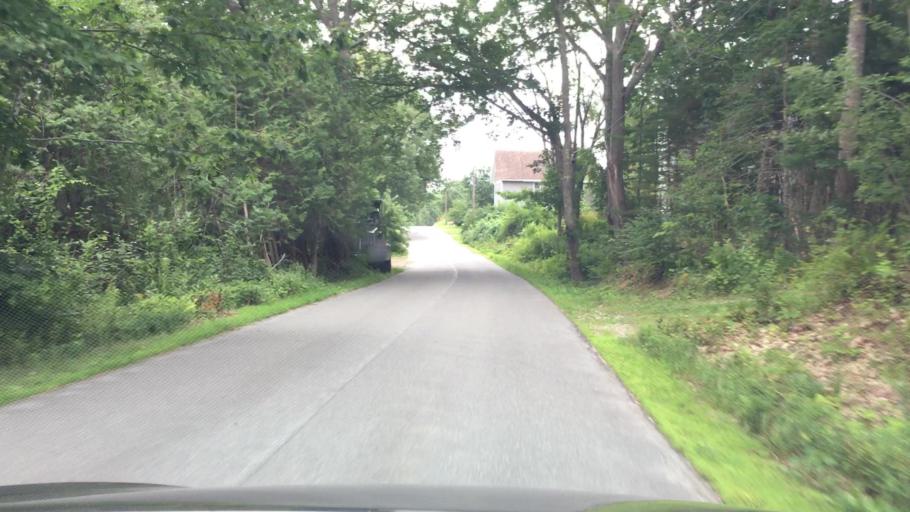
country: US
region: Maine
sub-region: Waldo County
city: Stockton Springs
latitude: 44.5085
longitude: -68.8104
